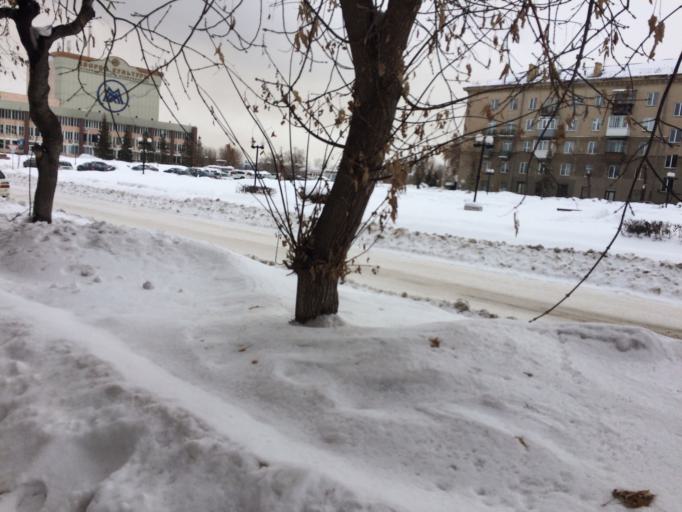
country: RU
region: Chelyabinsk
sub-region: Gorod Magnitogorsk
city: Magnitogorsk
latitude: 53.4184
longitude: 59.0003
